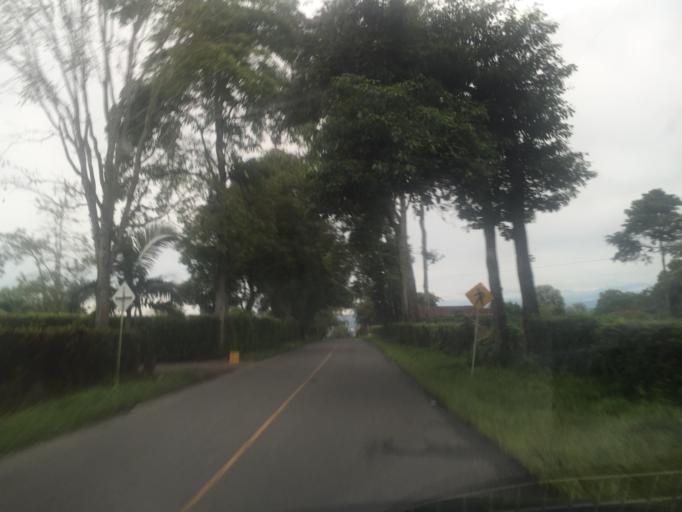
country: CO
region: Quindio
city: Montenegro
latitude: 4.5288
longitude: -75.7747
